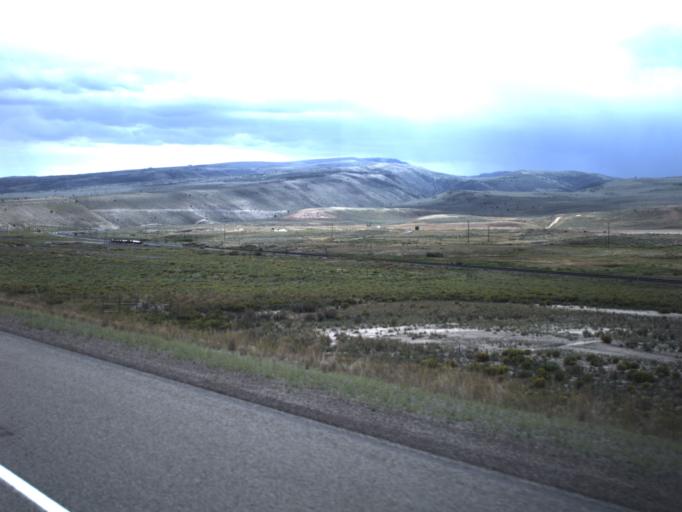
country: US
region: Utah
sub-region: Carbon County
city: Helper
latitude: 39.8557
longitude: -111.0181
